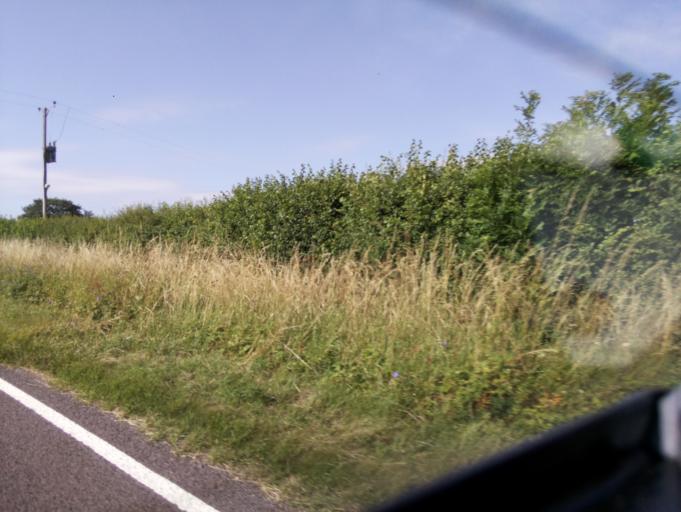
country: GB
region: England
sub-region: Oxfordshire
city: Faringdon
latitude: 51.6741
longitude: -1.5885
